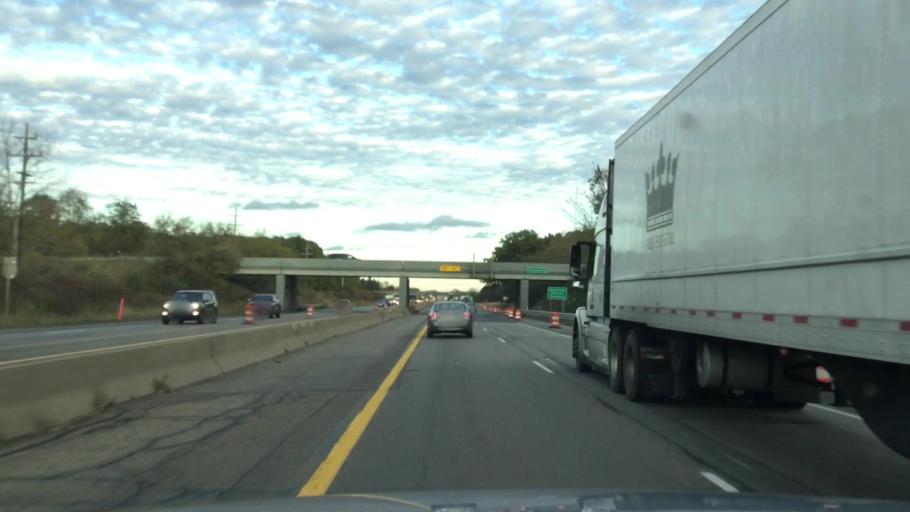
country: US
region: Michigan
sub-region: Jackson County
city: Jackson
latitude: 42.2690
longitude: -84.4845
